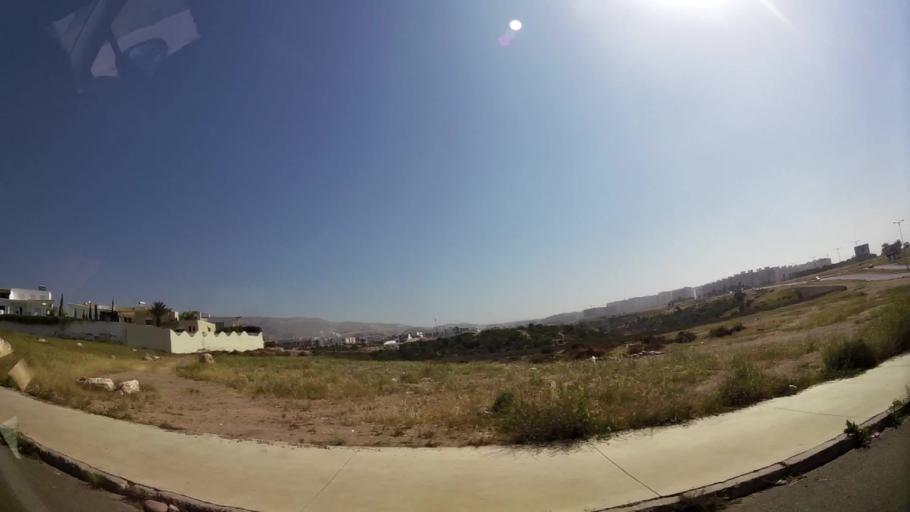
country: MA
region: Souss-Massa-Draa
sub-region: Agadir-Ida-ou-Tnan
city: Agadir
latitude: 30.4364
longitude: -9.5798
